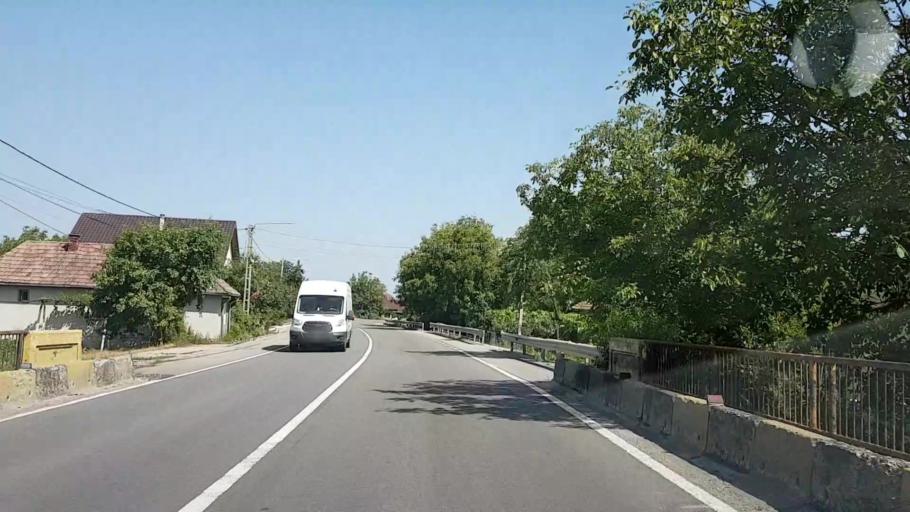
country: RO
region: Bistrita-Nasaud
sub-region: Comuna Uriu
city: Cristestii Ciceului
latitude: 47.1950
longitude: 24.0832
